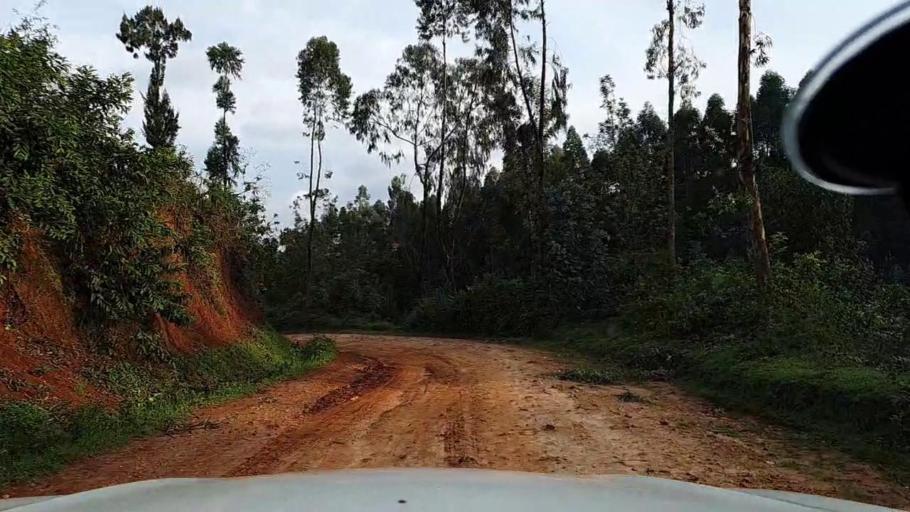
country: RW
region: Southern Province
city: Gitarama
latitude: -2.1882
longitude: 29.5743
